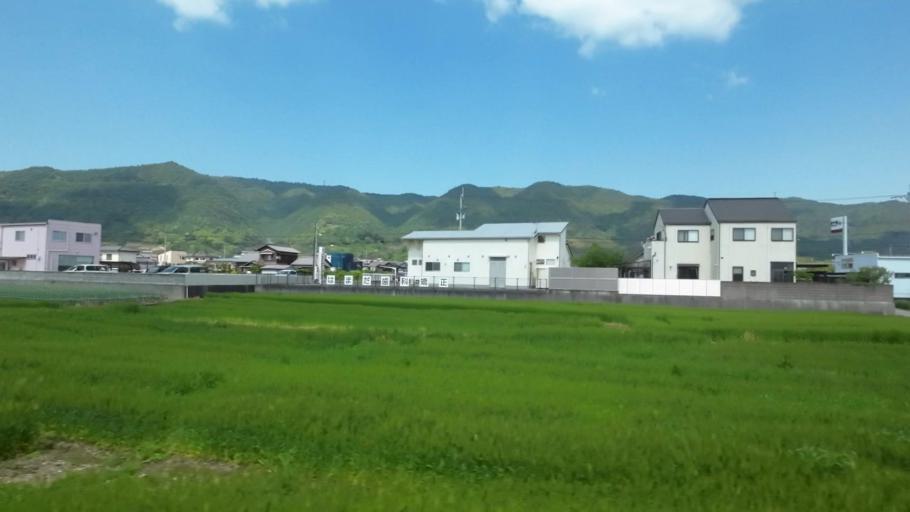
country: JP
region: Kagawa
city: Kan'onjicho
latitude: 34.1658
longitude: 133.6901
